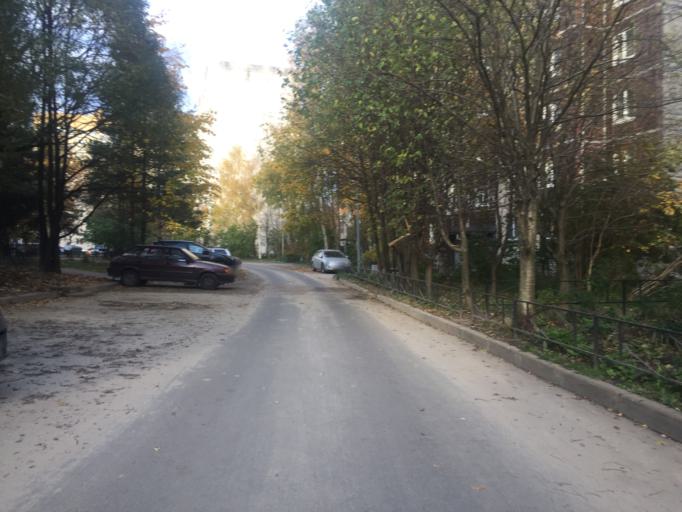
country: RU
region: Leningrad
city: Murino
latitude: 60.0457
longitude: 30.4662
